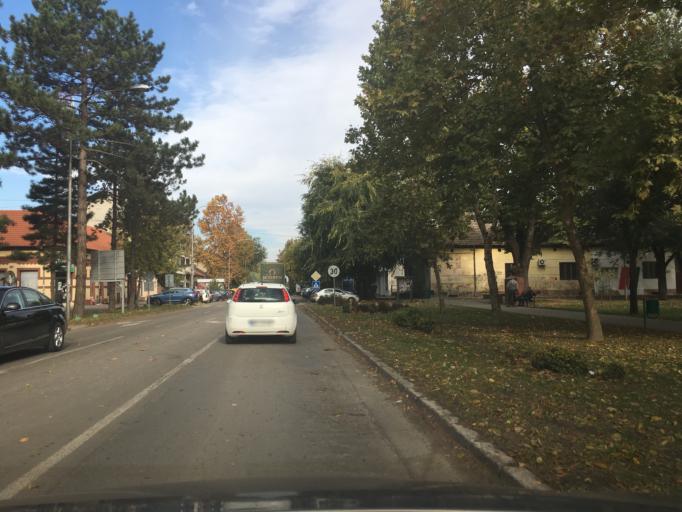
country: RS
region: Autonomna Pokrajina Vojvodina
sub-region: Juznobacki Okrug
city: Zabalj
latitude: 45.3731
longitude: 20.0633
